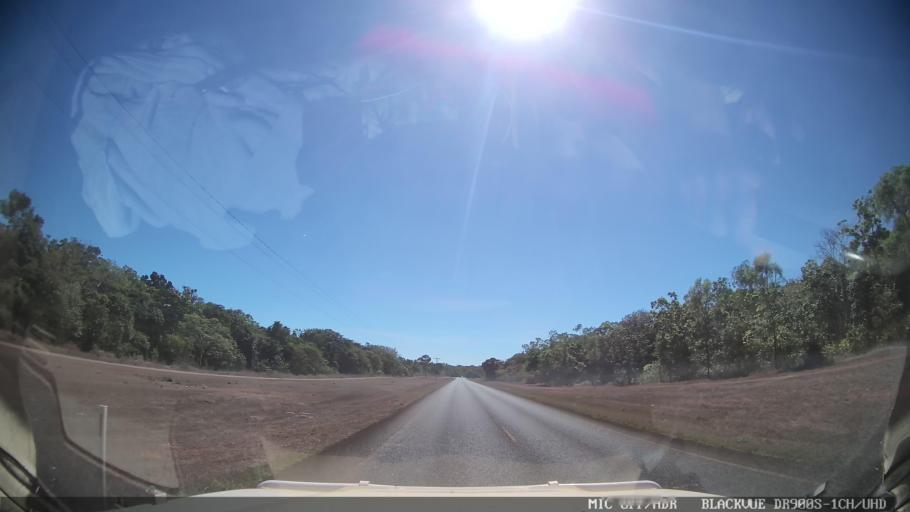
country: AU
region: Queensland
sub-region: Torres
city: Thursday Island
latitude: -10.9004
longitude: 142.3352
